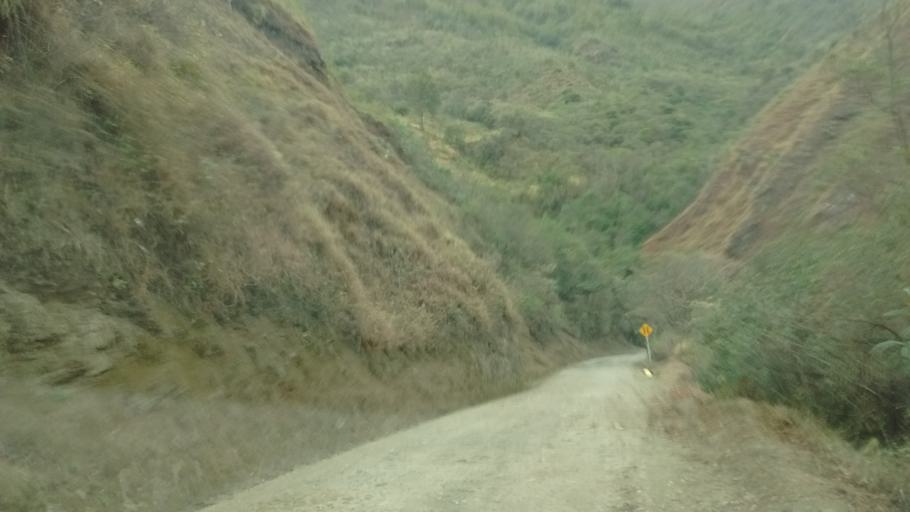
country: CO
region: Cauca
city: Almaguer
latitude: 1.8426
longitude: -76.9183
